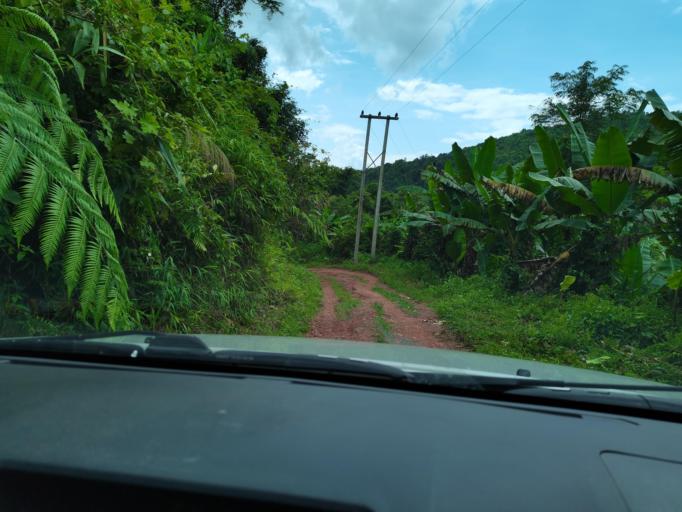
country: LA
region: Loungnamtha
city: Muang Nale
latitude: 20.5127
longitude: 101.0791
